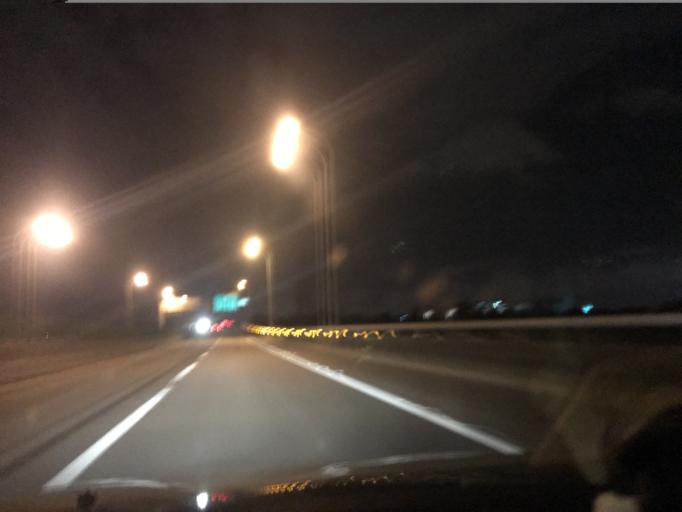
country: TW
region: Taiwan
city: Daxi
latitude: 24.8985
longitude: 121.2568
